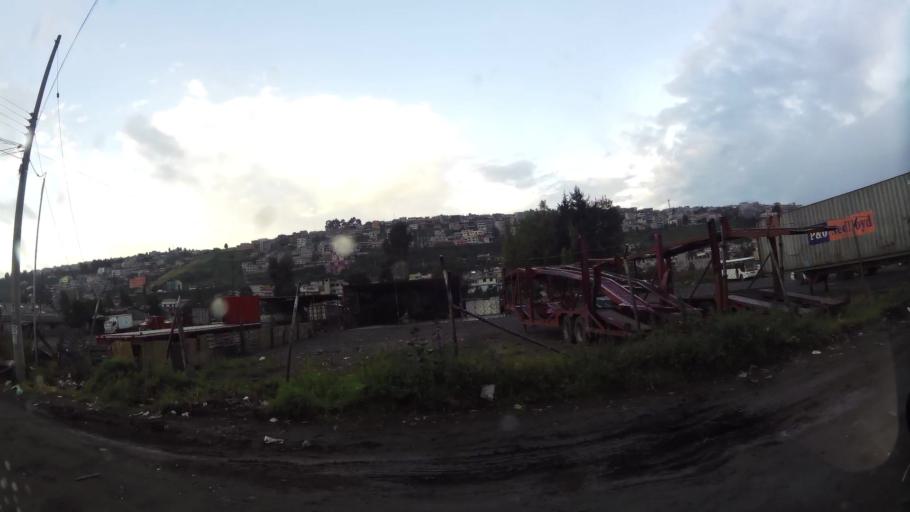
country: EC
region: Pichincha
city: Quito
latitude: -0.2978
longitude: -78.5381
